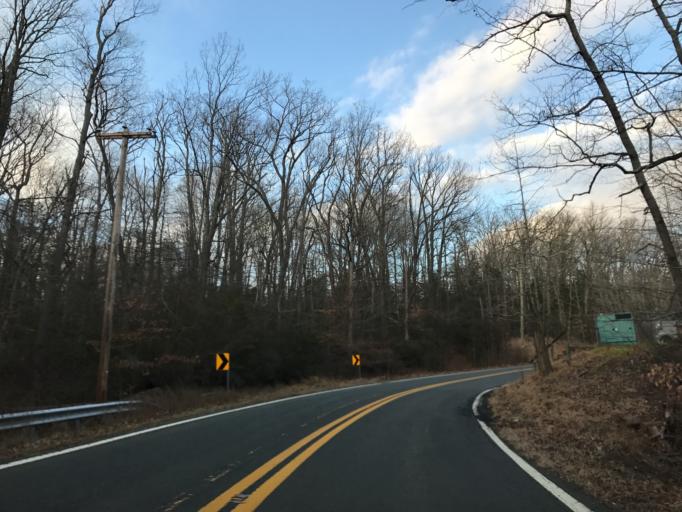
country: US
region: Maryland
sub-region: Cecil County
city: Charlestown
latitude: 39.4818
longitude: -75.9849
